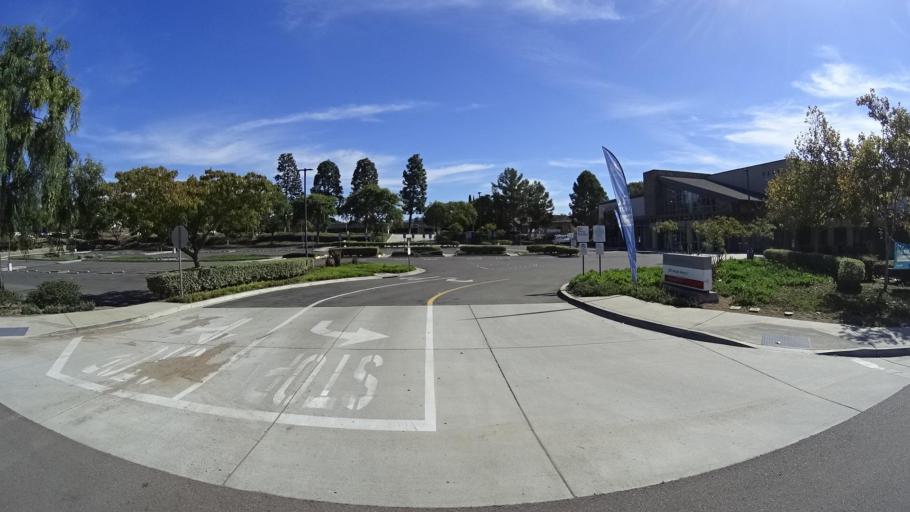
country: US
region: California
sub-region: San Diego County
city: Casa de Oro-Mount Helix
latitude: 32.7503
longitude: -116.9619
